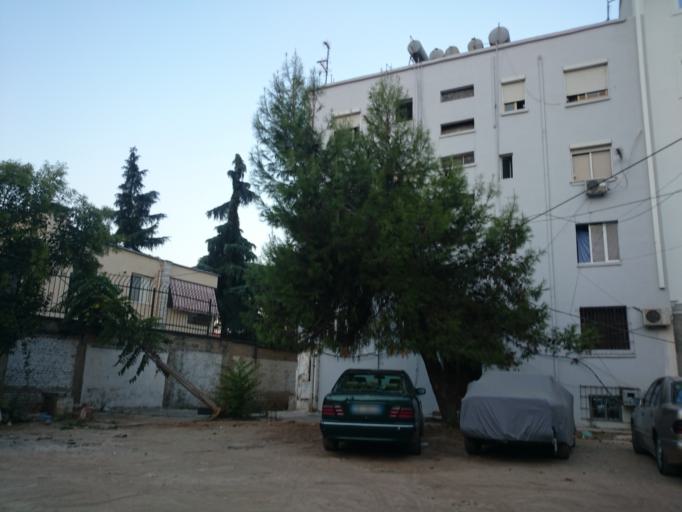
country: AL
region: Tirane
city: Tirana
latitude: 41.3314
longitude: 19.8081
